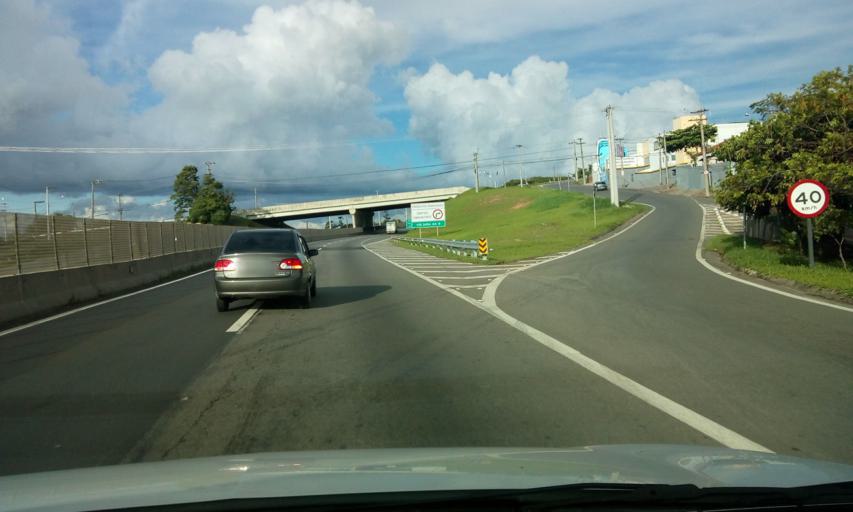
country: BR
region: Sao Paulo
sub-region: Jundiai
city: Jundiai
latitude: -23.1641
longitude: -46.9103
